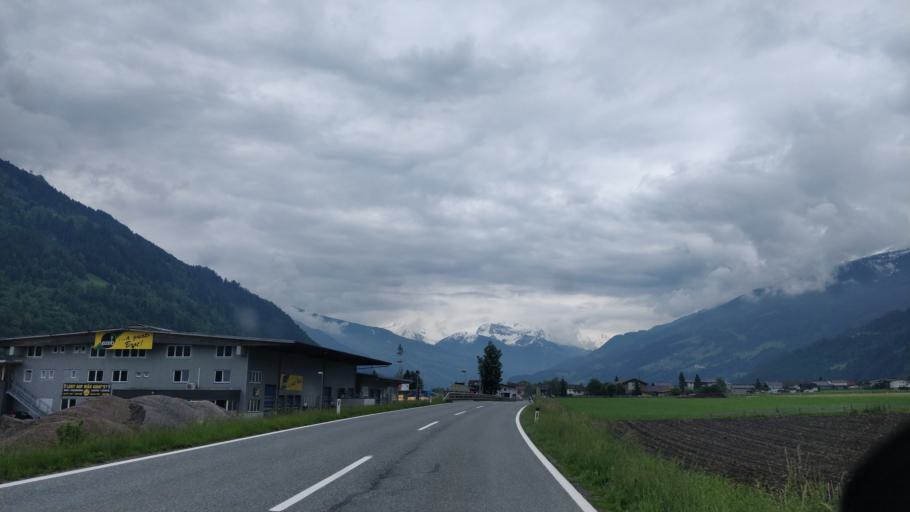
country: AT
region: Tyrol
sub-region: Politischer Bezirk Schwaz
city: Hart im Zillertal
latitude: 47.3344
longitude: 11.8613
